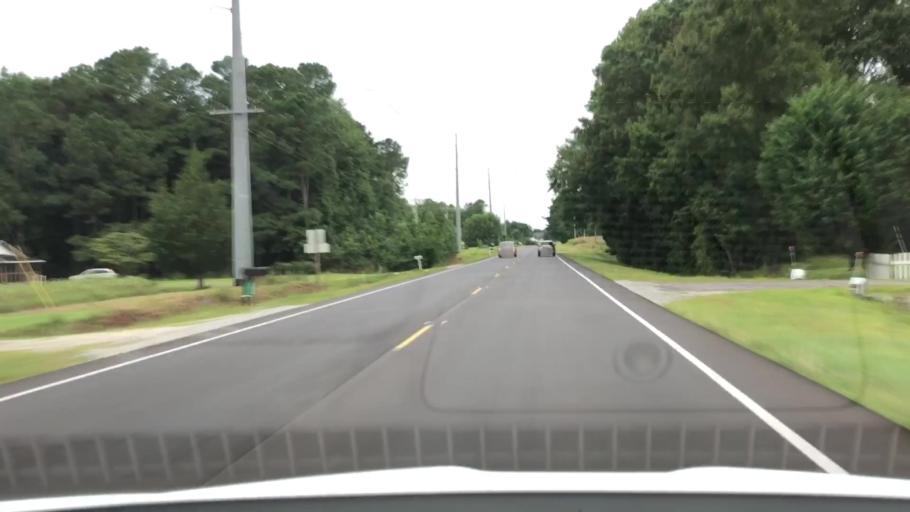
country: US
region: North Carolina
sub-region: Jones County
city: Maysville
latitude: 34.8336
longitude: -77.1650
